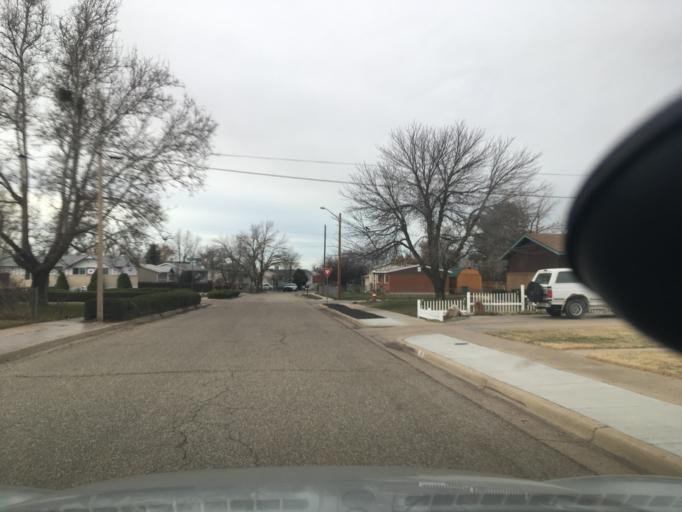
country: US
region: Utah
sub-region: Davis County
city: Layton
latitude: 41.0733
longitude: -111.9618
